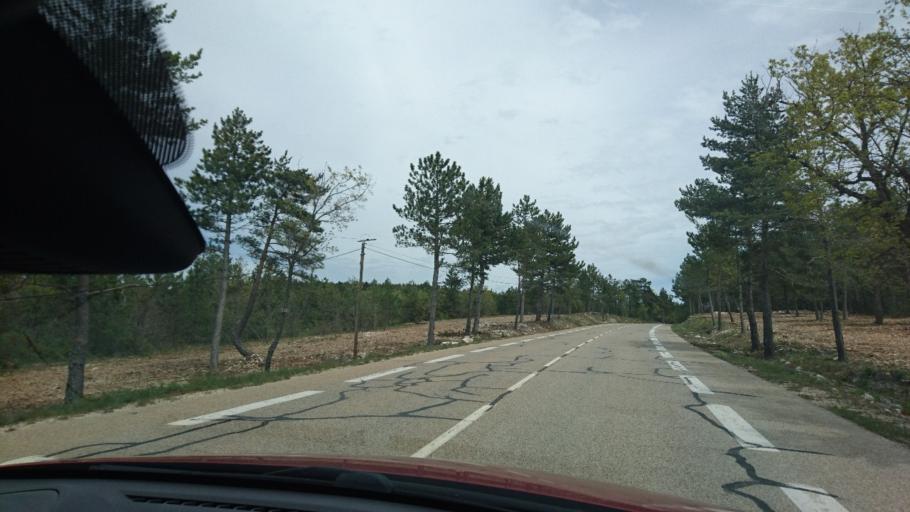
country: FR
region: Provence-Alpes-Cote d'Azur
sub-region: Departement du Vaucluse
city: Sault
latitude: 44.0940
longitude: 5.3194
